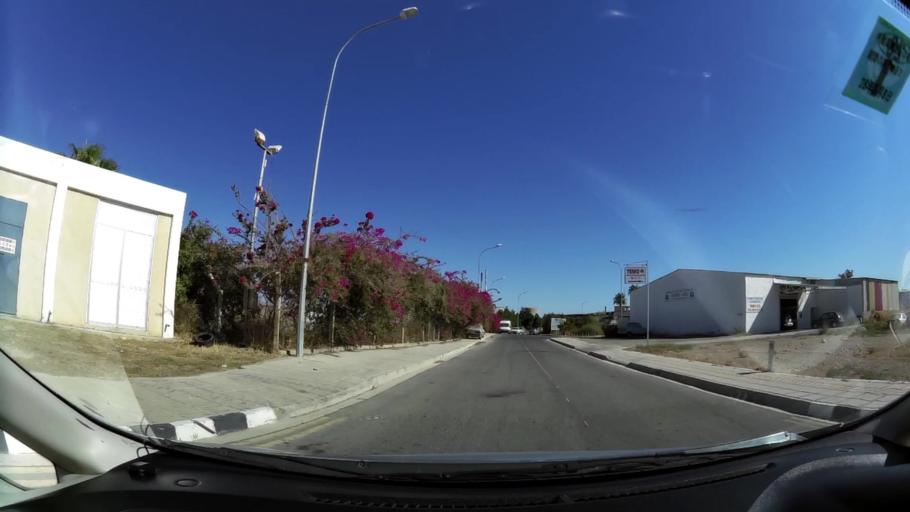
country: CY
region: Larnaka
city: Livadia
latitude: 34.9382
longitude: 33.6392
